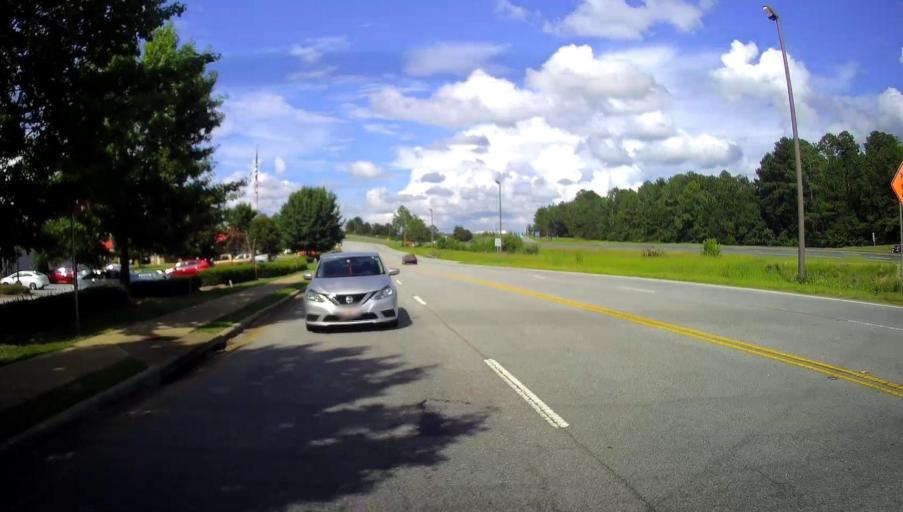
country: US
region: Georgia
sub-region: Muscogee County
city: Columbus
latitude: 32.5376
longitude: -84.8748
